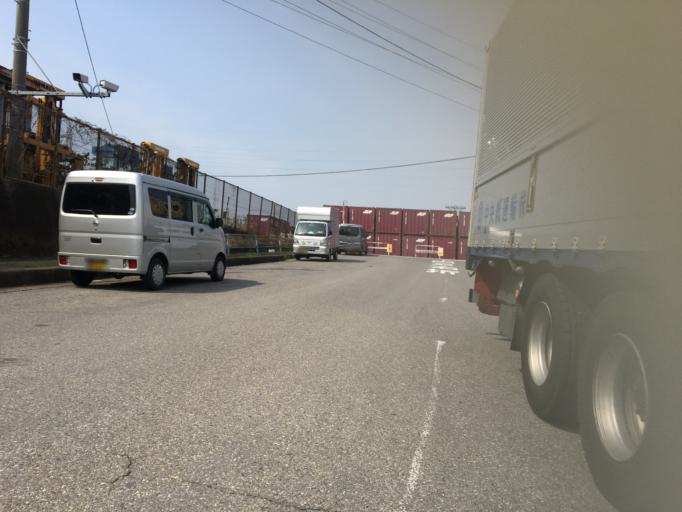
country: JP
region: Saitama
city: Shiki
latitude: 35.8038
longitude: 139.5534
